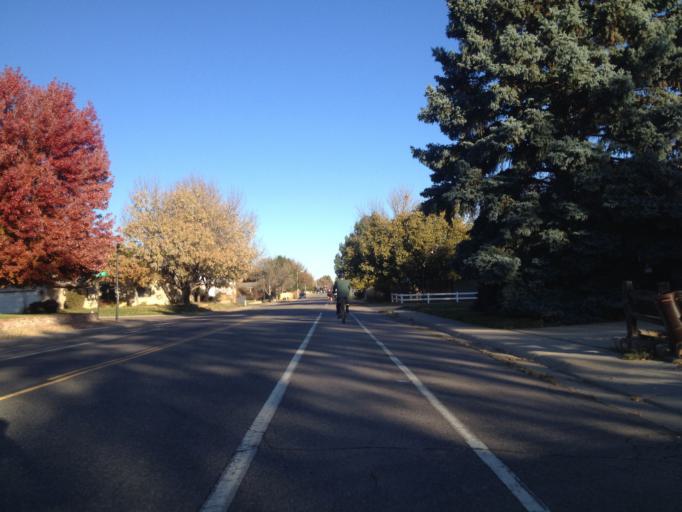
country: US
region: Colorado
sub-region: Boulder County
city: Longmont
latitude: 40.1849
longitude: -105.1235
